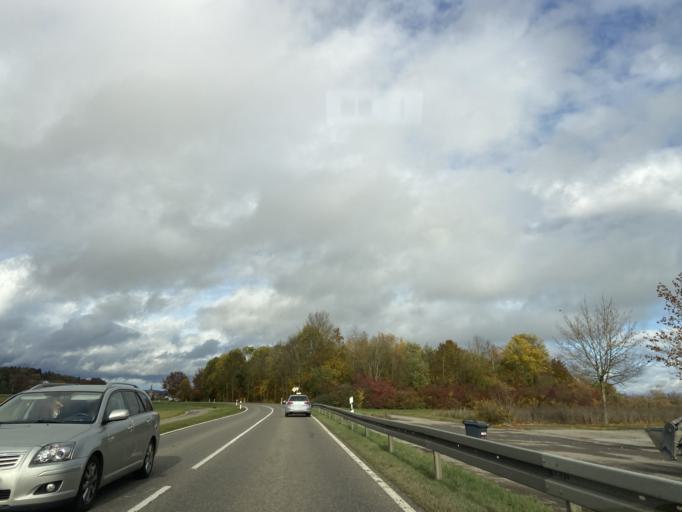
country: DE
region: Baden-Wuerttemberg
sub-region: Tuebingen Region
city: Inzigkofen
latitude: 48.0475
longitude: 9.1392
